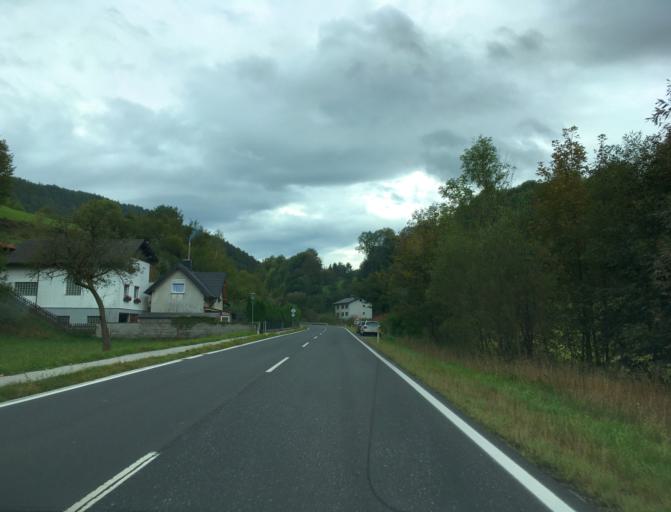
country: AT
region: Lower Austria
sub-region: Politischer Bezirk Neunkirchen
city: Edlitz
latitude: 47.5860
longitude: 16.1460
